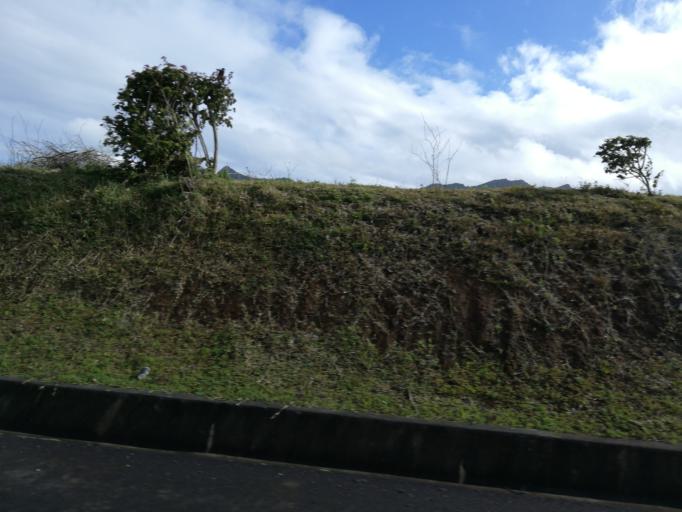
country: MU
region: Moka
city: Saint Pierre
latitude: -20.2337
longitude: 57.5123
